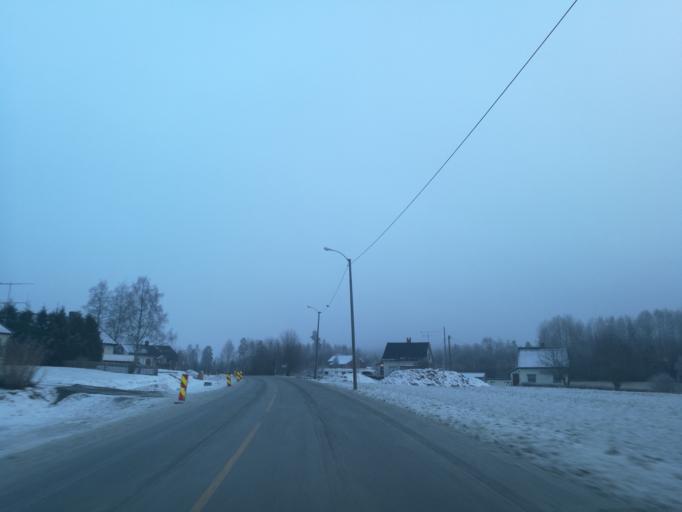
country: NO
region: Hedmark
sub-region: Kongsvinger
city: Kongsvinger
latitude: 60.2595
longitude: 12.0760
